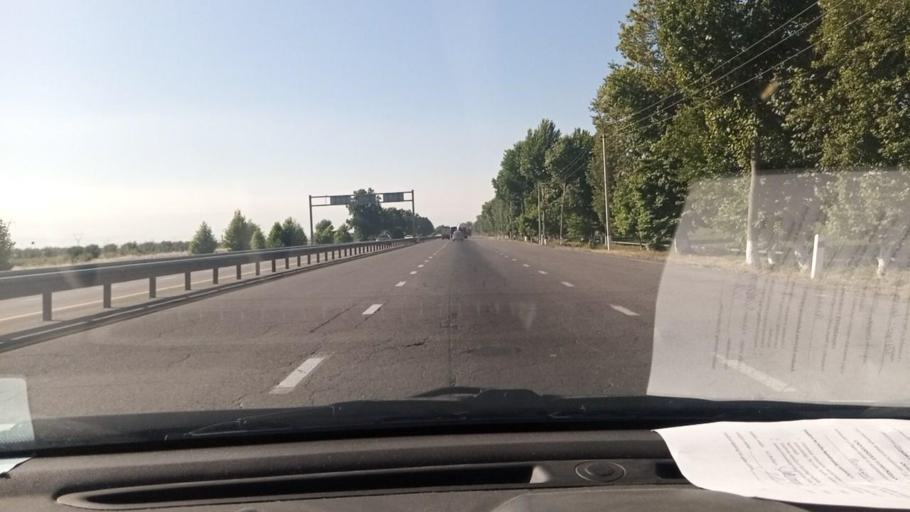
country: UZ
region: Toshkent Shahri
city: Bektemir
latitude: 41.1801
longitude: 69.4075
